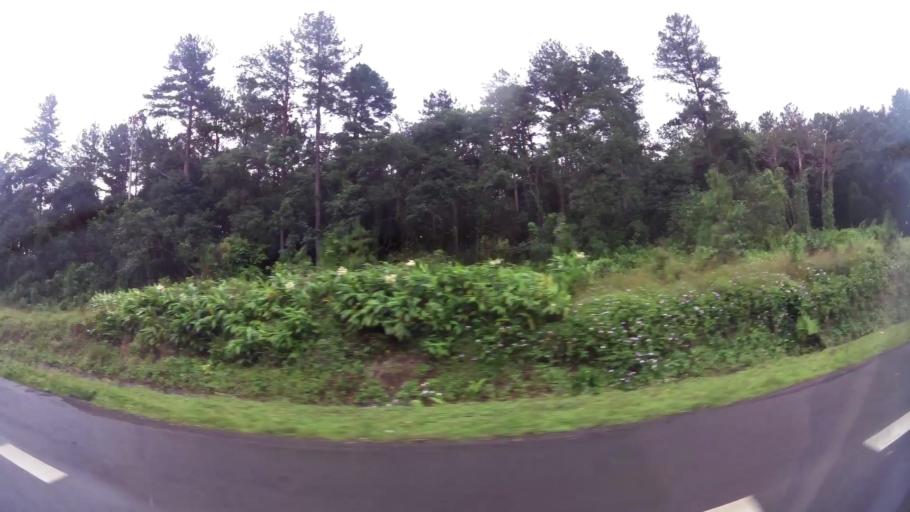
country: MU
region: Plaines Wilhems
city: Curepipe
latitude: -20.3091
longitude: 57.5415
